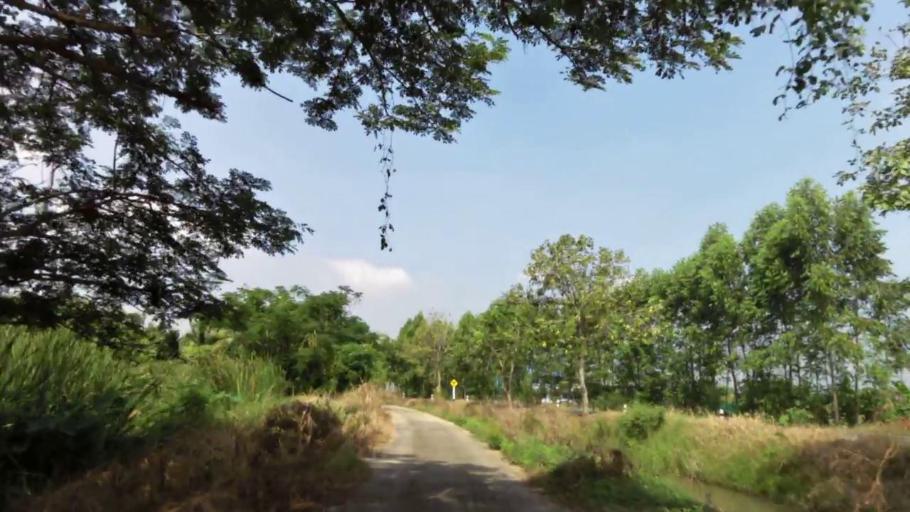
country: TH
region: Ang Thong
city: Pho Thong
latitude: 14.6125
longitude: 100.3955
